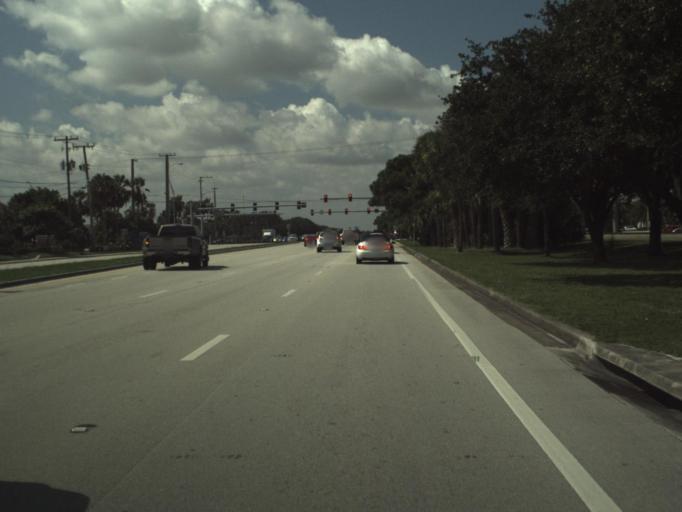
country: US
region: Florida
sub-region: Palm Beach County
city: Jupiter
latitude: 26.9359
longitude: -80.0936
